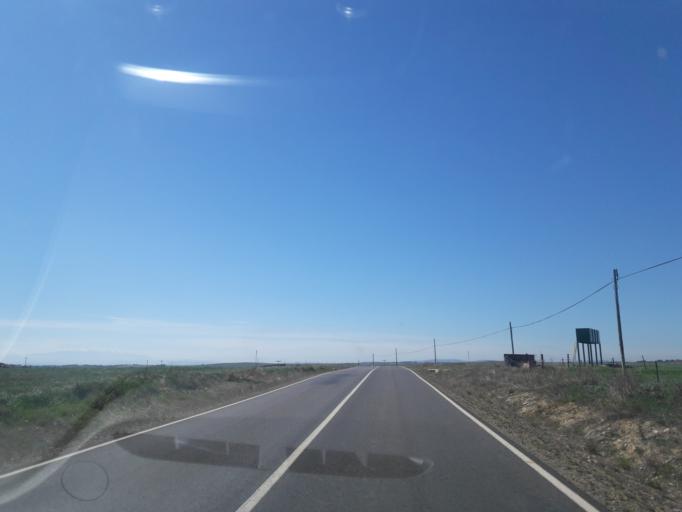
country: ES
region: Castille and Leon
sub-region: Provincia de Salamanca
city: Martinamor
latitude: 40.8116
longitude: -5.5955
